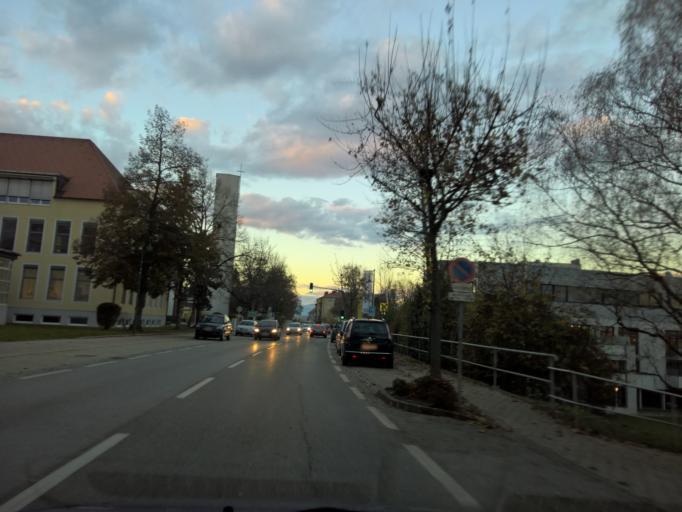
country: AT
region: Styria
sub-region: Politischer Bezirk Graz-Umgebung
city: Kalsdorf bei Graz
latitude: 46.9628
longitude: 15.4791
